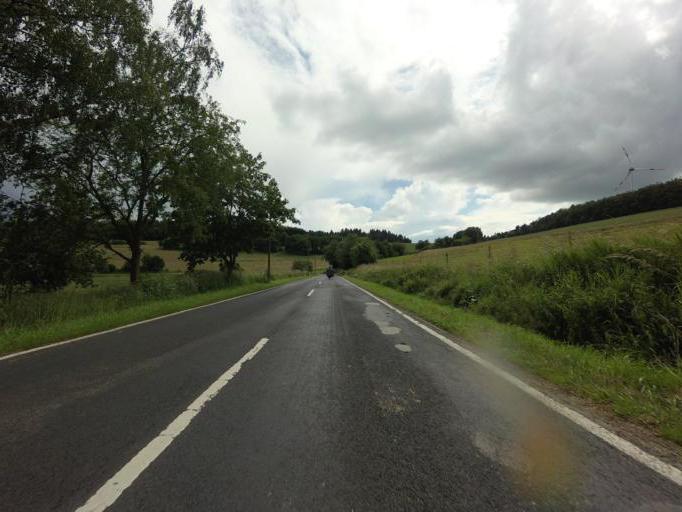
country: DE
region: Rheinland-Pfalz
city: Landkern
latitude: 50.2058
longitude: 7.1571
